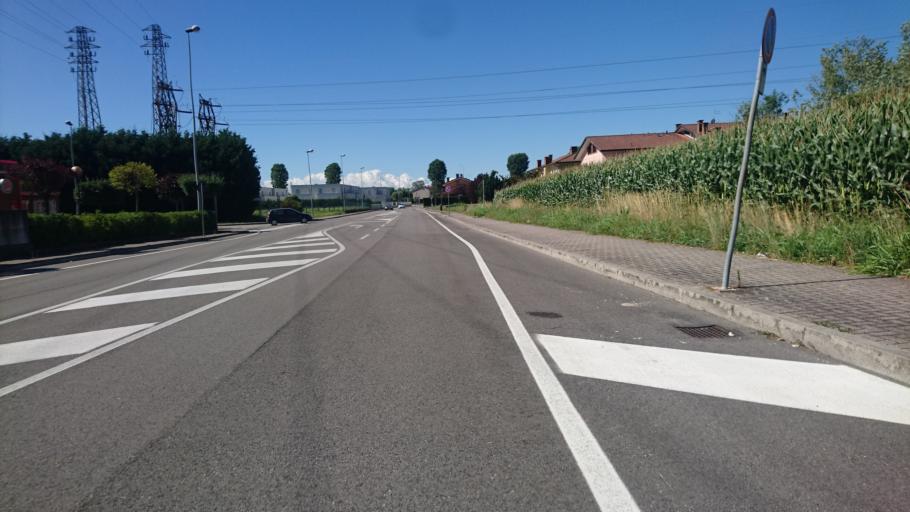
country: IT
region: Veneto
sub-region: Provincia di Padova
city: Sant'Angelo di Piove di Sacco
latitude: 45.3036
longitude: 12.0198
